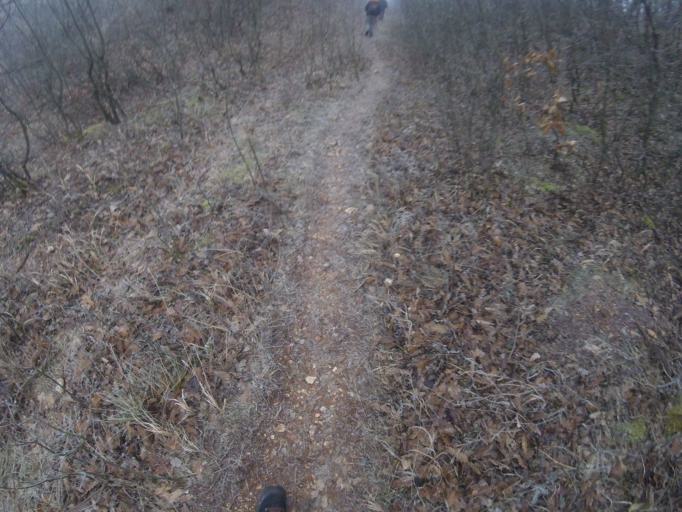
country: HU
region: Fejer
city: Zamoly
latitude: 47.3726
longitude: 18.3912
